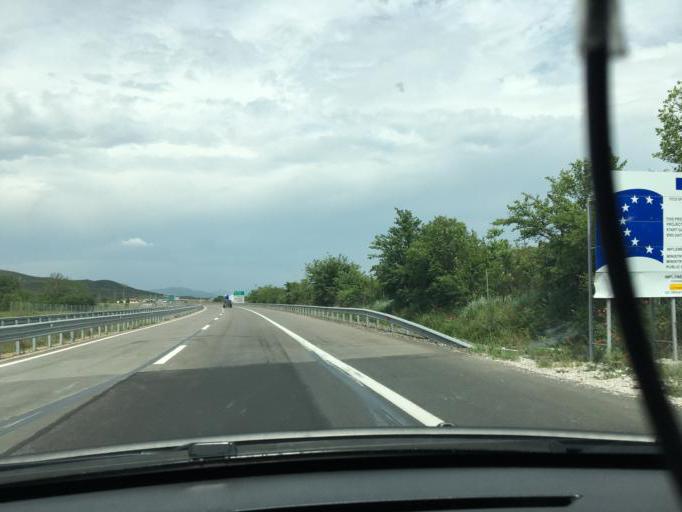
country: MK
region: Gevgelija
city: Miravci
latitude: 41.2535
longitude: 22.4791
